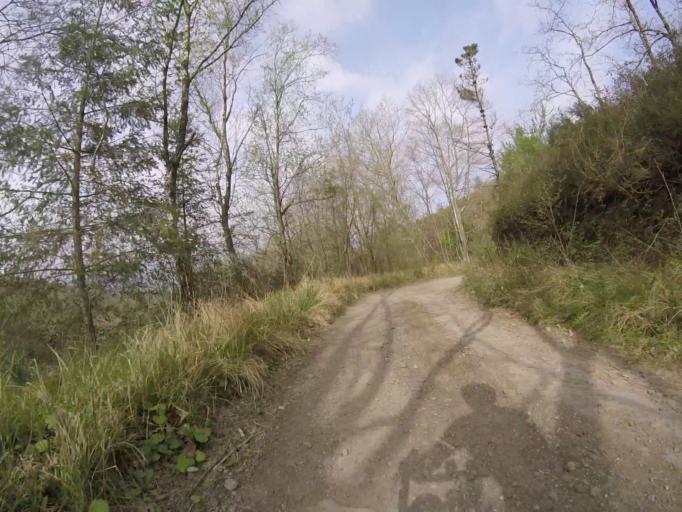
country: ES
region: Basque Country
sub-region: Provincia de Guipuzcoa
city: Usurbil
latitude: 43.2433
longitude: -2.0784
